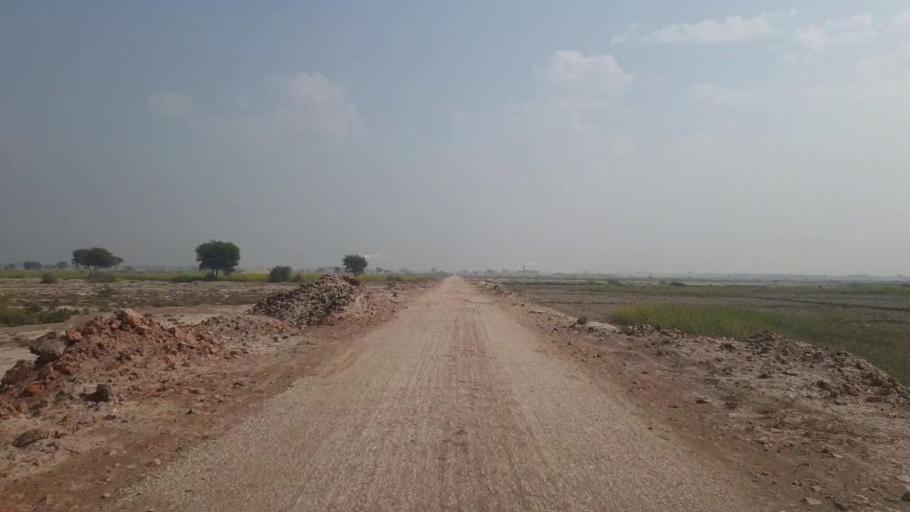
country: PK
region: Sindh
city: Hala
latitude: 25.7839
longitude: 68.4183
